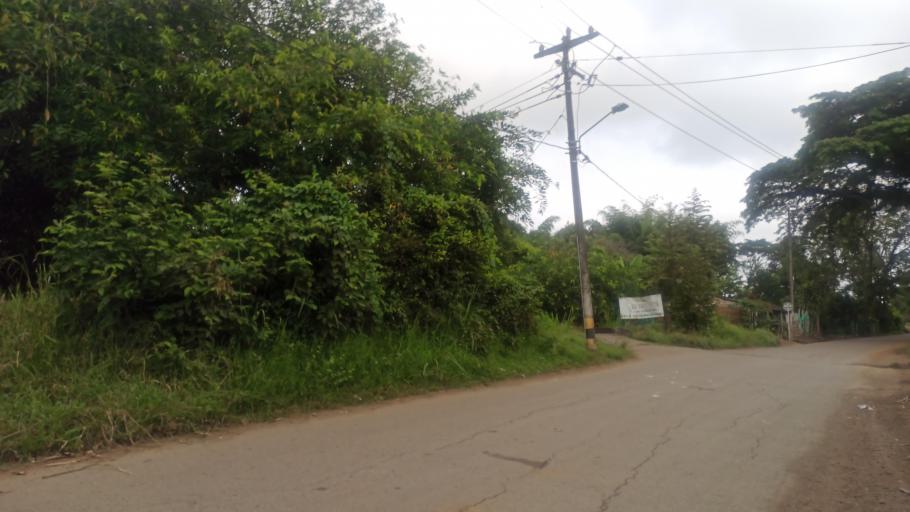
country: CO
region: Valle del Cauca
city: Jamundi
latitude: 3.2003
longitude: -76.5094
